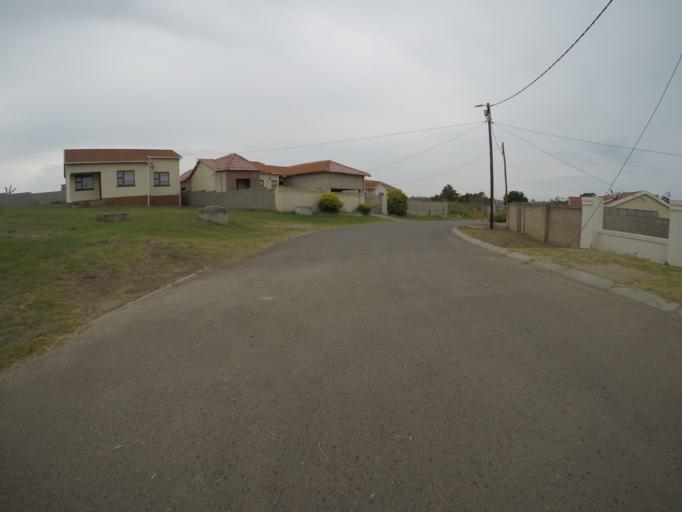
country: ZA
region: Eastern Cape
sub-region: Buffalo City Metropolitan Municipality
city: East London
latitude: -33.0036
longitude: 27.8525
